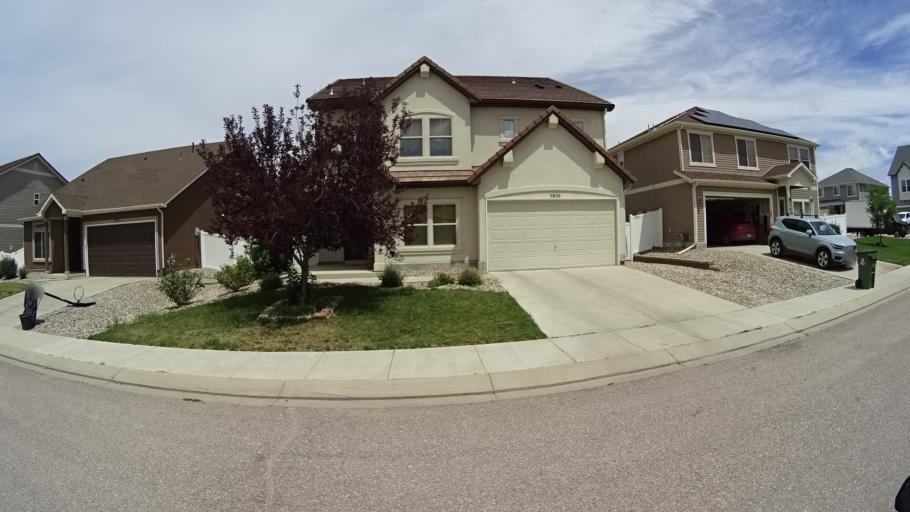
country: US
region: Colorado
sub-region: El Paso County
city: Fountain
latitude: 38.6949
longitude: -104.6793
